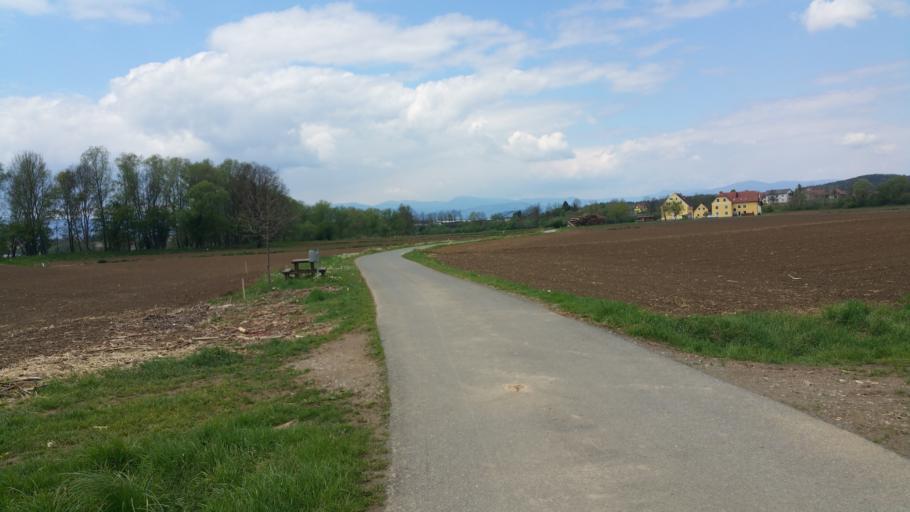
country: AT
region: Styria
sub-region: Politischer Bezirk Leibnitz
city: Gleinstatten
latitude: 46.7548
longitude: 15.3879
